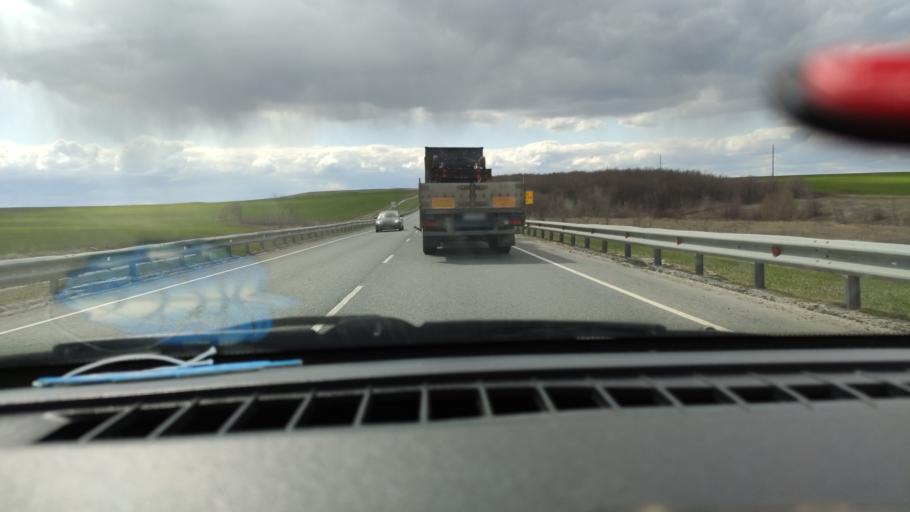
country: RU
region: Saratov
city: Alekseyevka
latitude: 52.2239
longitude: 47.9008
